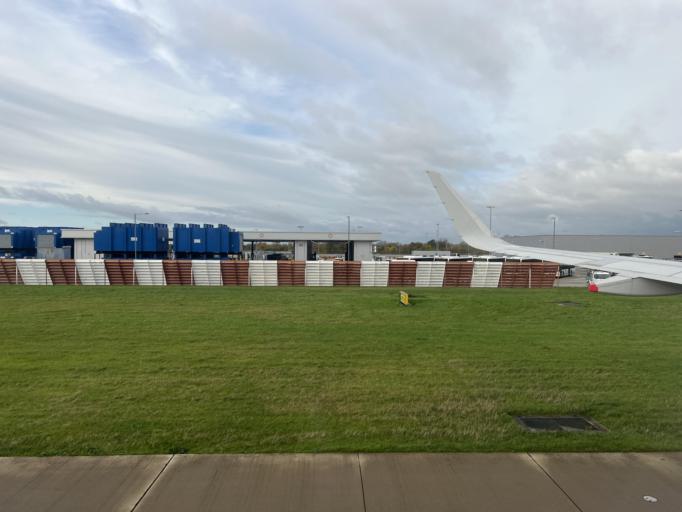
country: GB
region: England
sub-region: Buckinghamshire
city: Iver
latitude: 51.4669
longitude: -0.4875
